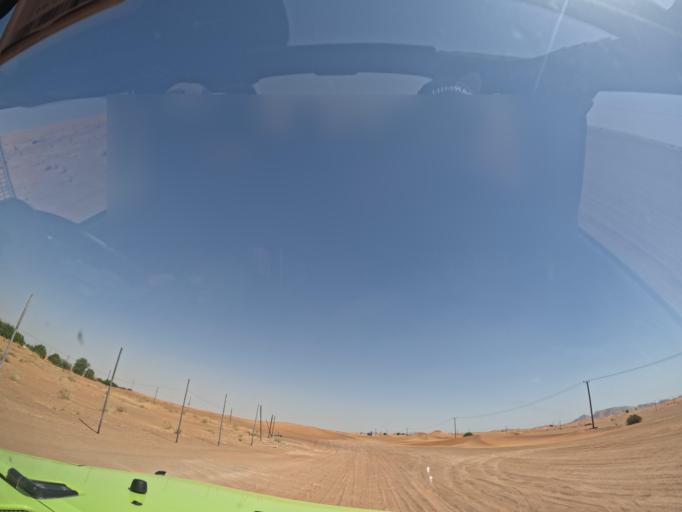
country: AE
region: Ash Shariqah
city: Adh Dhayd
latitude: 25.0070
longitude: 55.7380
